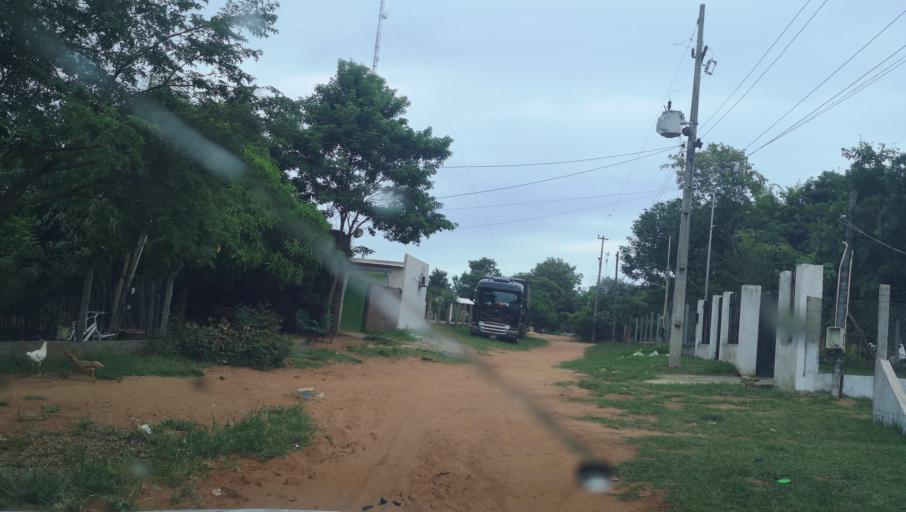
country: PY
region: San Pedro
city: Capiibary
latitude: -24.7288
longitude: -56.0152
